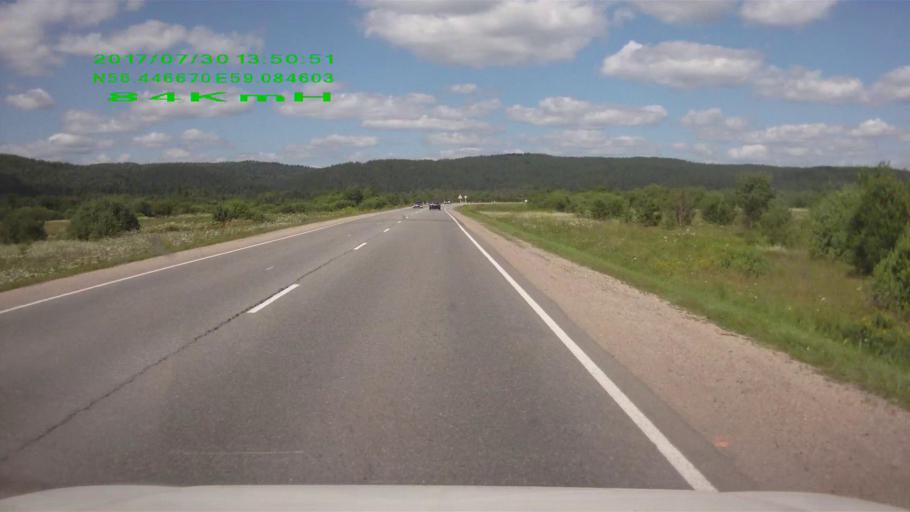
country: RU
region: Sverdlovsk
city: Mikhaylovsk
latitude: 56.4469
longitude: 59.0841
